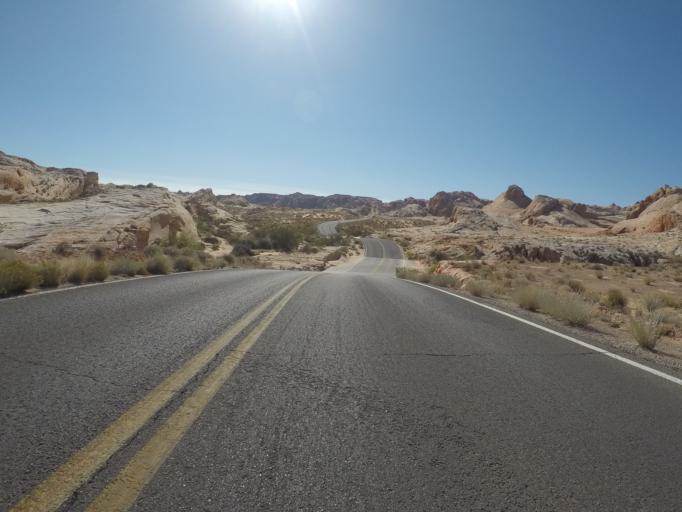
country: US
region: Nevada
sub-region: Clark County
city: Moapa Valley
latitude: 36.4800
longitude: -114.5265
